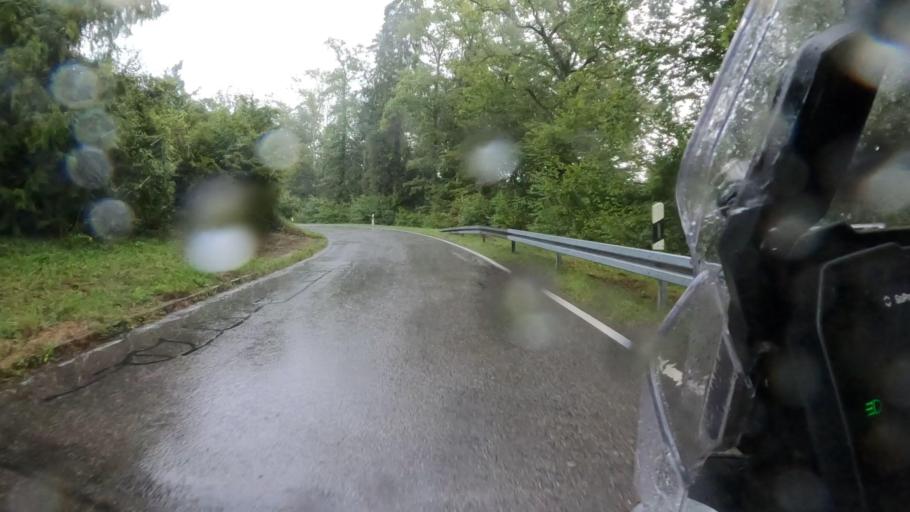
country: DE
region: Baden-Wuerttemberg
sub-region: Freiburg Region
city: Jestetten
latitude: 47.6438
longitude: 8.5926
